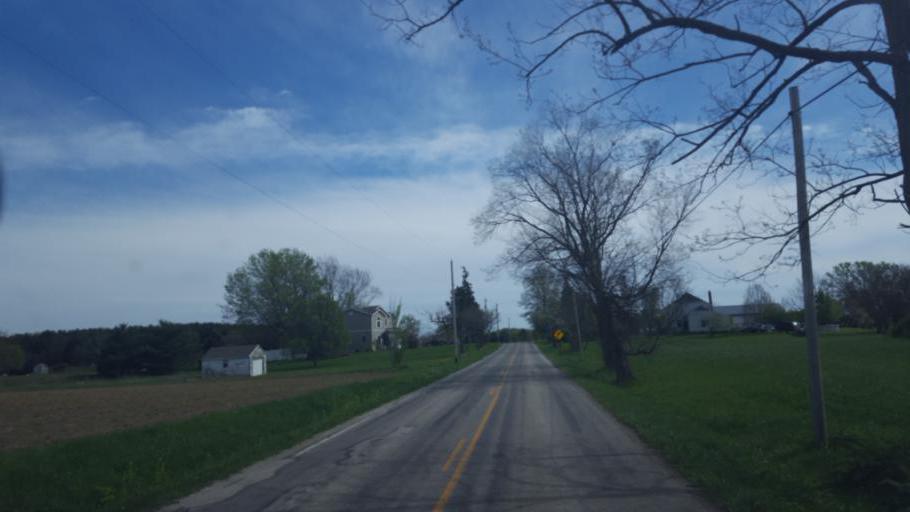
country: US
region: Ohio
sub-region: Richland County
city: Shelby
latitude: 40.8916
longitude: -82.6229
